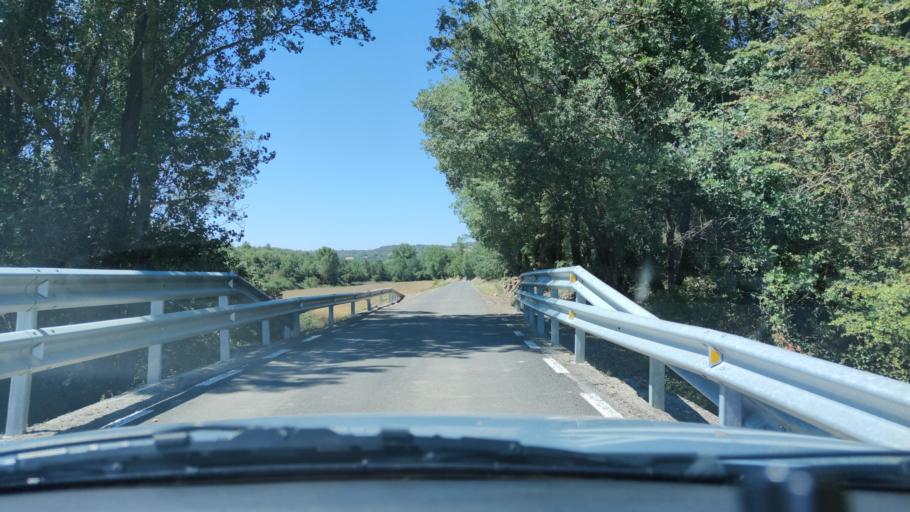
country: ES
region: Catalonia
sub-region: Provincia de Lleida
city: Tora de Riubregos
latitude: 41.9071
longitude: 1.4483
